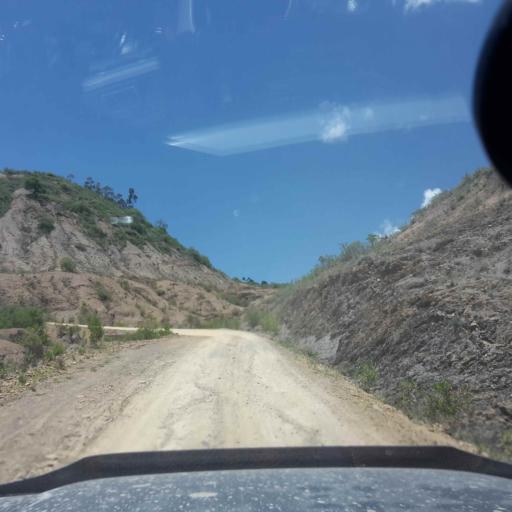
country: BO
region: Cochabamba
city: Totora
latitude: -17.7676
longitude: -65.2388
